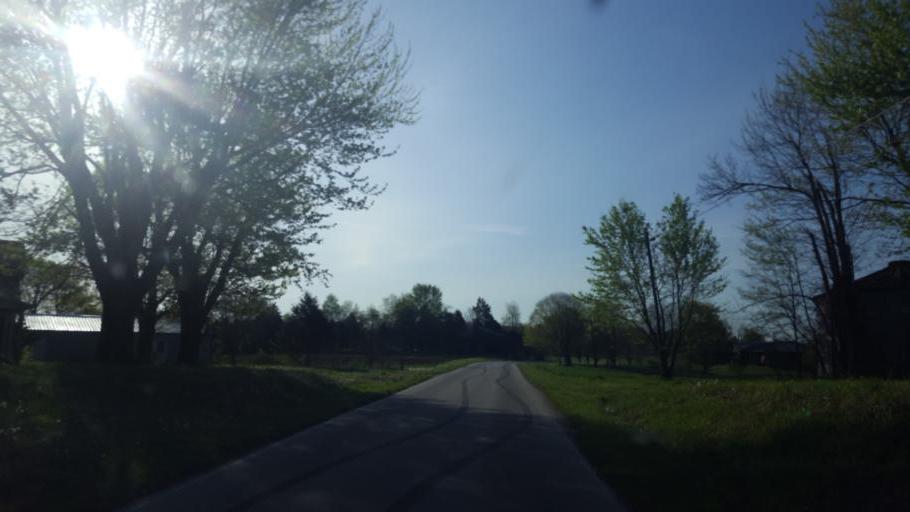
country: US
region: Kentucky
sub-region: Larue County
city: Hodgenville
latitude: 37.4755
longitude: -85.9186
